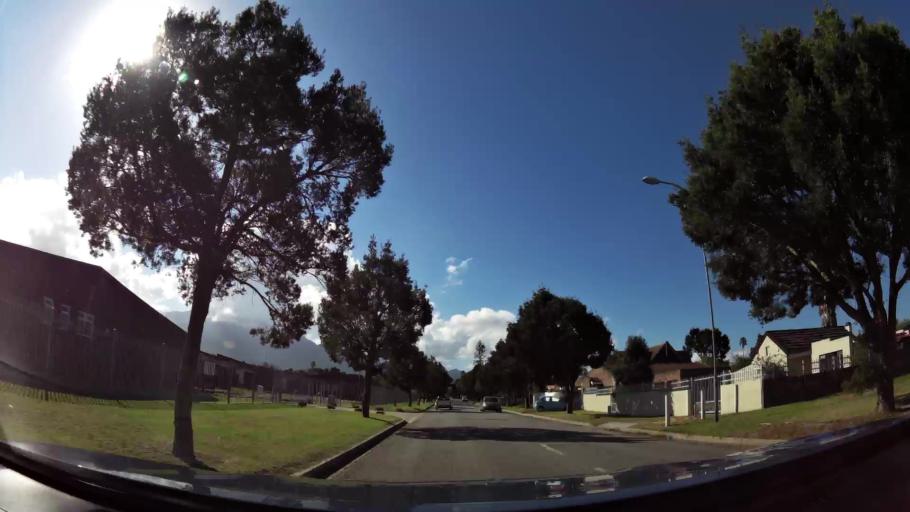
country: ZA
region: Western Cape
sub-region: Eden District Municipality
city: George
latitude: -33.9744
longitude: 22.4519
